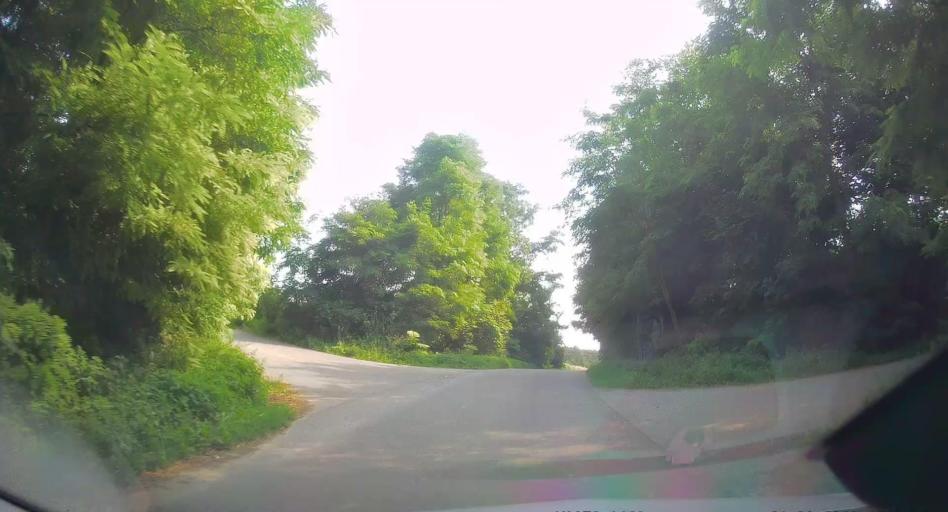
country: PL
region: Lesser Poland Voivodeship
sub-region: Powiat bochenski
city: Dziewin
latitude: 50.1547
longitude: 20.4631
